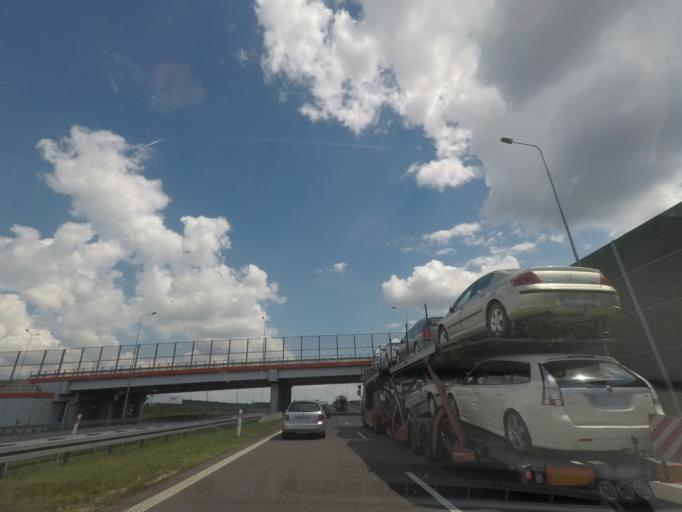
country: PL
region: Masovian Voivodeship
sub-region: Powiat grodziski
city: Grodzisk Mazowiecki
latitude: 52.1460
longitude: 20.6164
